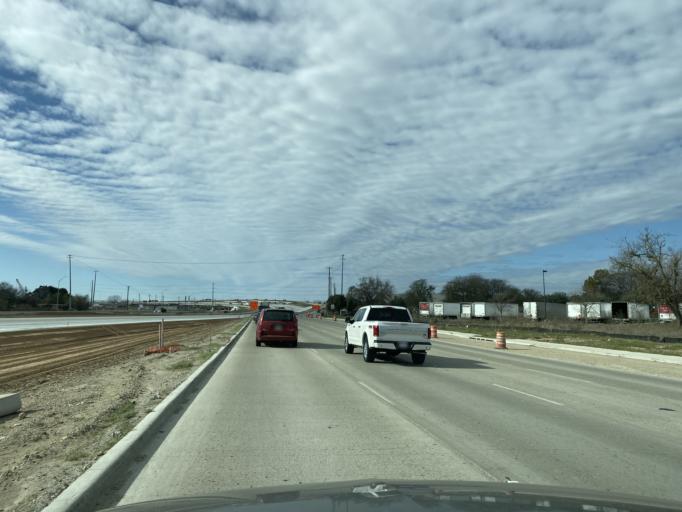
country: US
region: Texas
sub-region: Travis County
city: Austin
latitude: 30.2518
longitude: -97.6828
